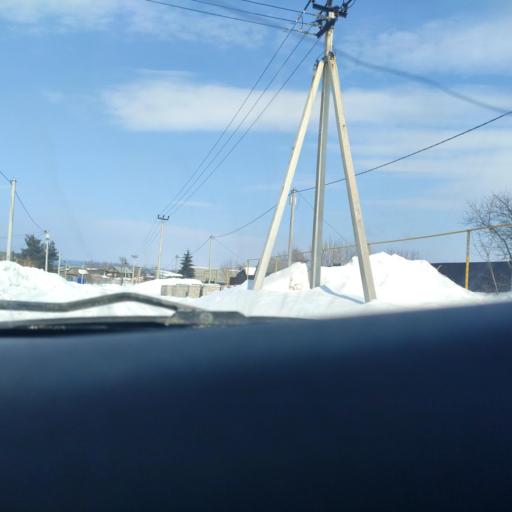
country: RU
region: Samara
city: Rozhdestveno
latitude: 53.2440
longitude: 50.0627
